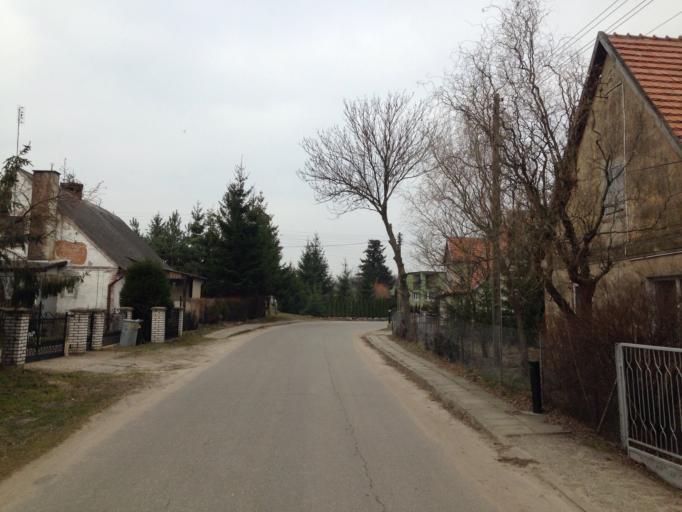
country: PL
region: Pomeranian Voivodeship
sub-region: Powiat kwidzynski
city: Sadlinki
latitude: 53.7386
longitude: 18.8251
